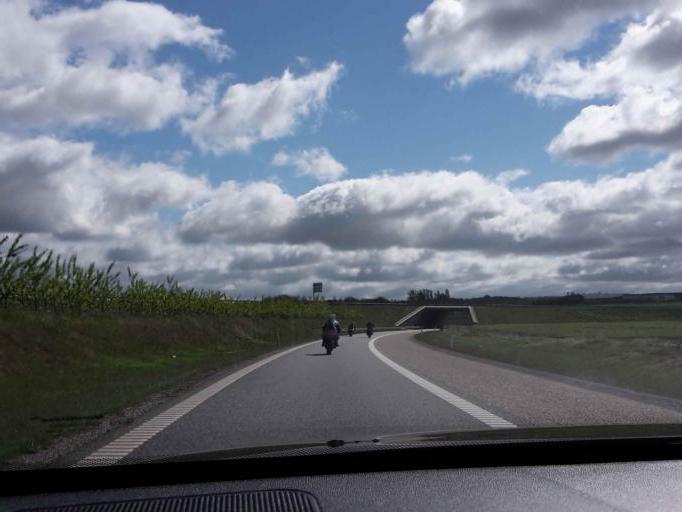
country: DK
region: Central Jutland
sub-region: Favrskov Kommune
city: Soften
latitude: 56.2224
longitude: 10.1217
